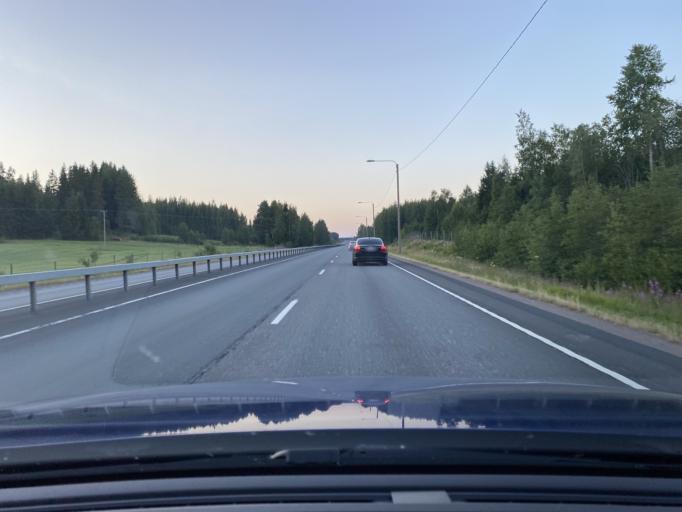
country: FI
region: Pirkanmaa
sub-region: Luoteis-Pirkanmaa
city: Ikaalinen
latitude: 61.8788
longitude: 22.9699
